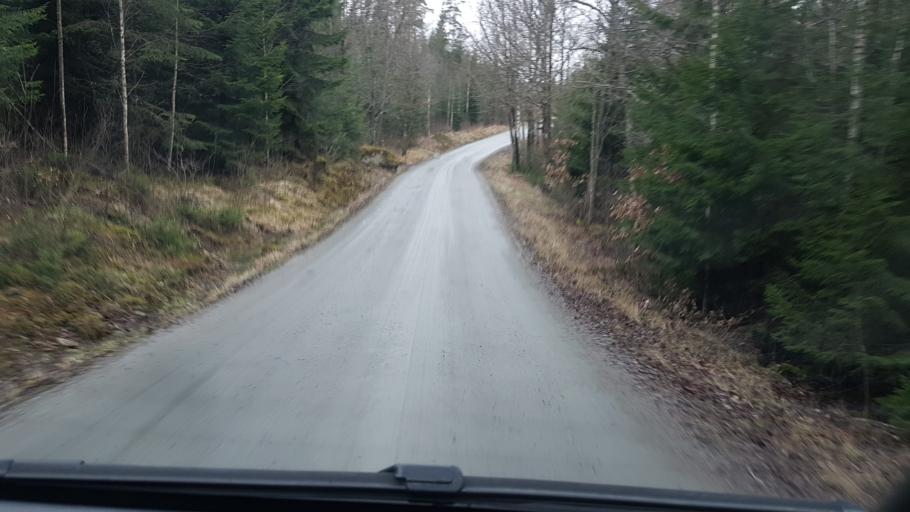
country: SE
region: Vaestra Goetaland
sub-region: Lerums Kommun
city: Stenkullen
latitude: 57.7976
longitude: 12.3886
